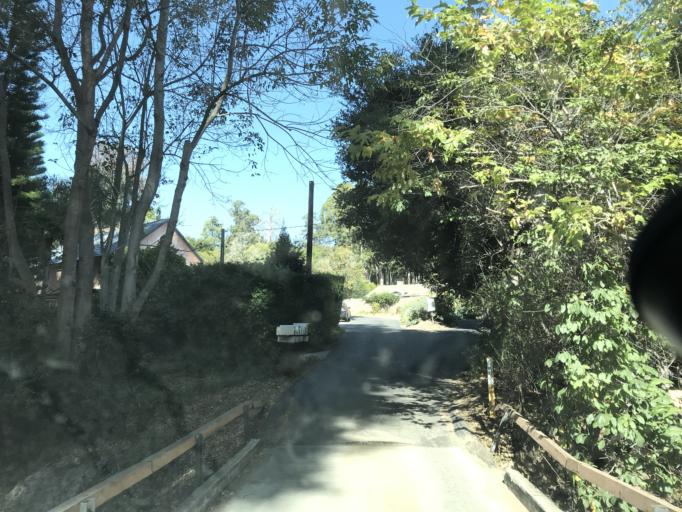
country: US
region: California
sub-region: Santa Barbara County
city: Goleta
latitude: 34.4527
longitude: -119.8008
